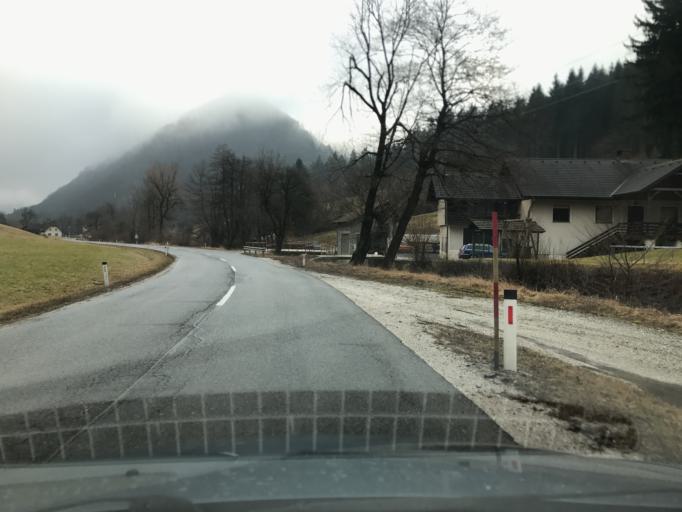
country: SI
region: Gornji Grad
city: Gornji Grad
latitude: 46.2140
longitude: 14.8549
